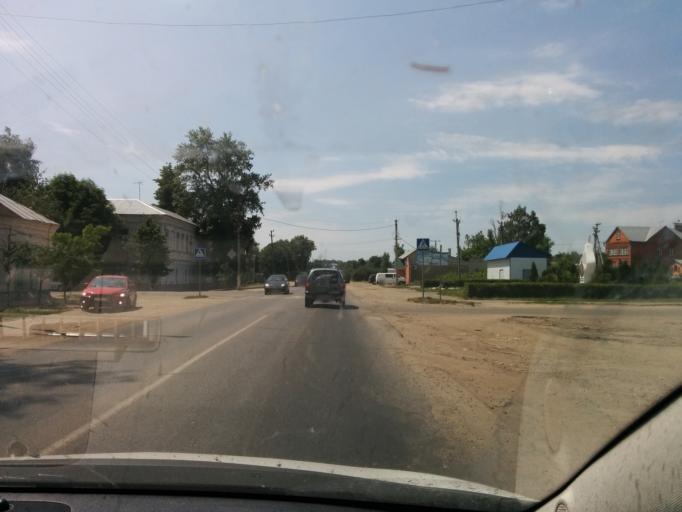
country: RU
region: Tambov
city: Morshansk
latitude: 53.4475
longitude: 41.8091
